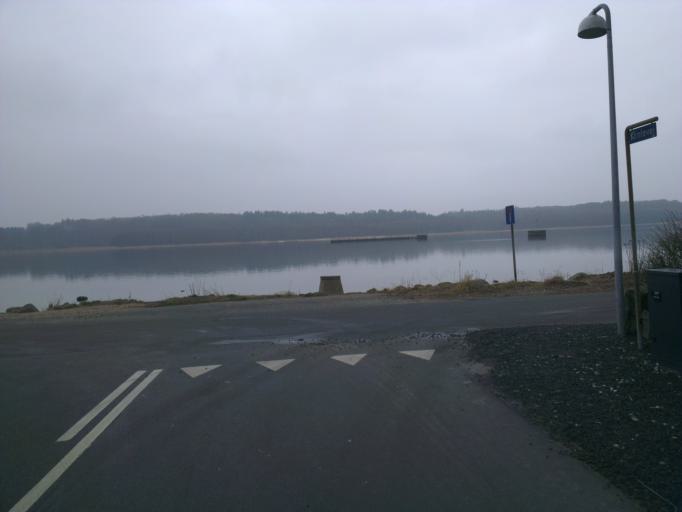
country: DK
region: Capital Region
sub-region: Frederikssund Kommune
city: Frederikssund
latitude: 55.8453
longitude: 12.0436
